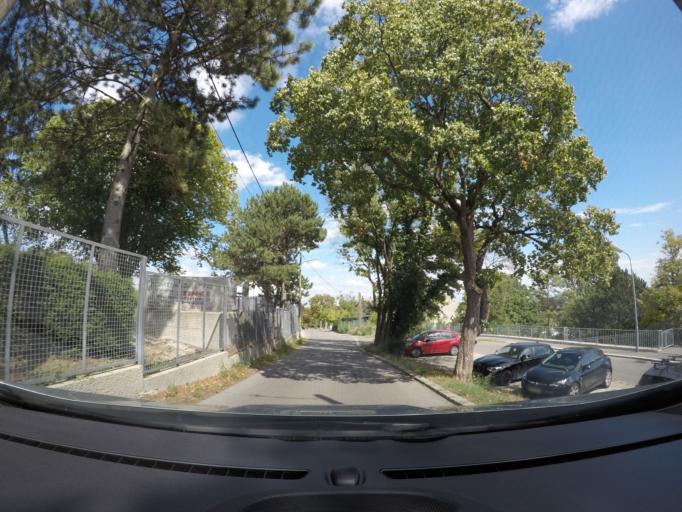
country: AT
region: Lower Austria
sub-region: Politischer Bezirk Modling
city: Perchtoldsdorf
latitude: 48.1776
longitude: 16.2619
